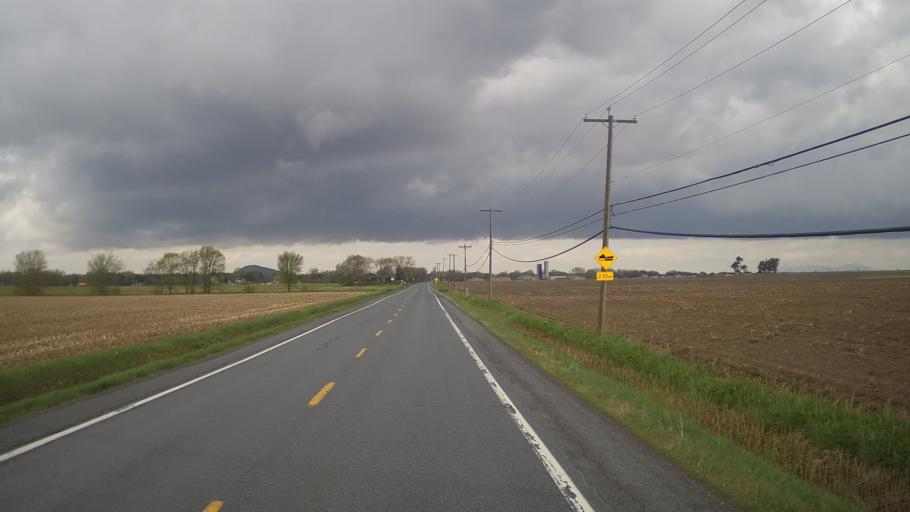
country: CA
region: Quebec
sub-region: Monteregie
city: Farnham
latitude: 45.3136
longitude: -73.0512
